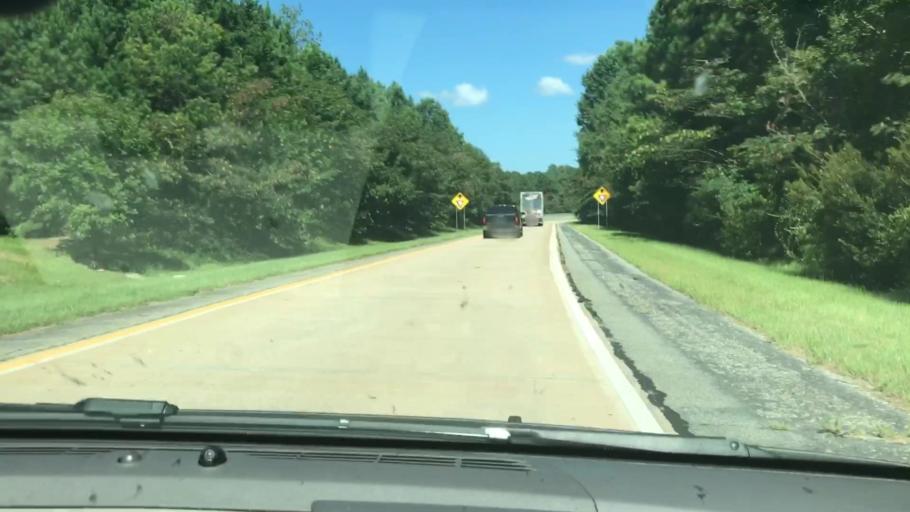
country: US
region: Alabama
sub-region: Russell County
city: Phenix City
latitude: 32.5476
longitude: -84.9592
